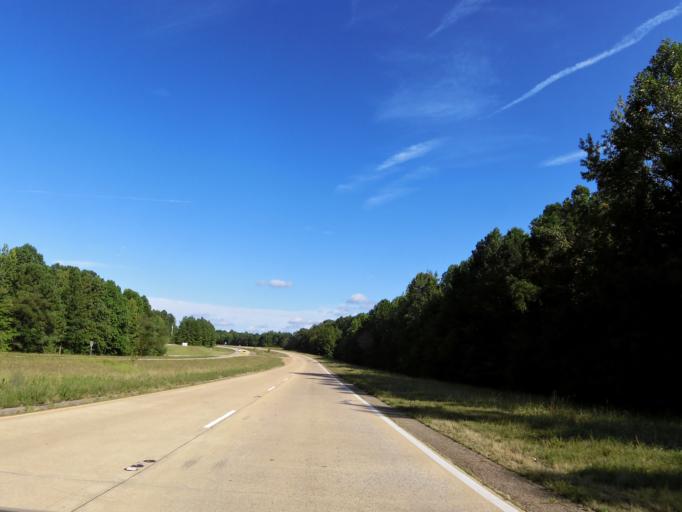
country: US
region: Mississippi
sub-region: Tishomingo County
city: Iuka
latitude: 34.7830
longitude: -88.1808
